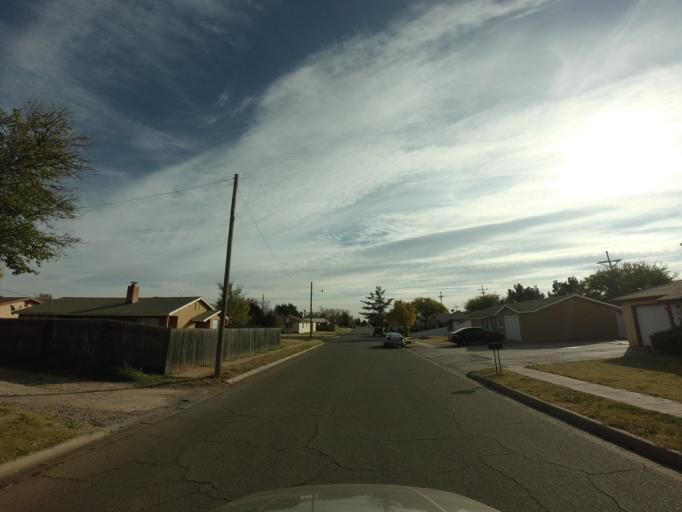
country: US
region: New Mexico
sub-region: Curry County
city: Clovis
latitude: 34.4275
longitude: -103.2224
